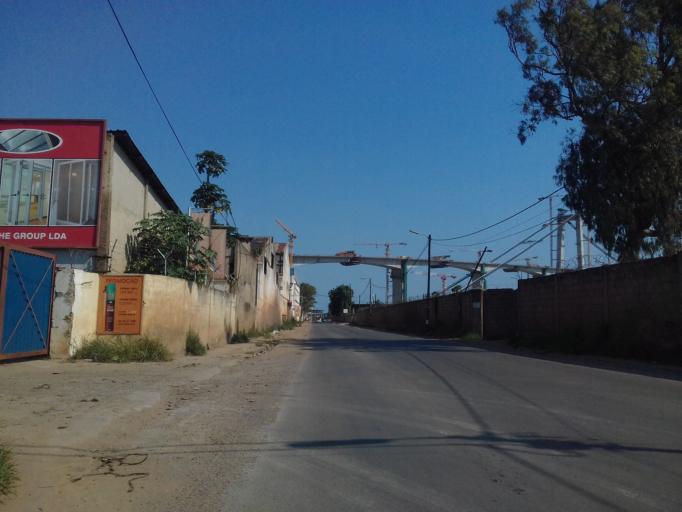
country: MZ
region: Maputo City
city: Maputo
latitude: -25.9624
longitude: 32.5571
